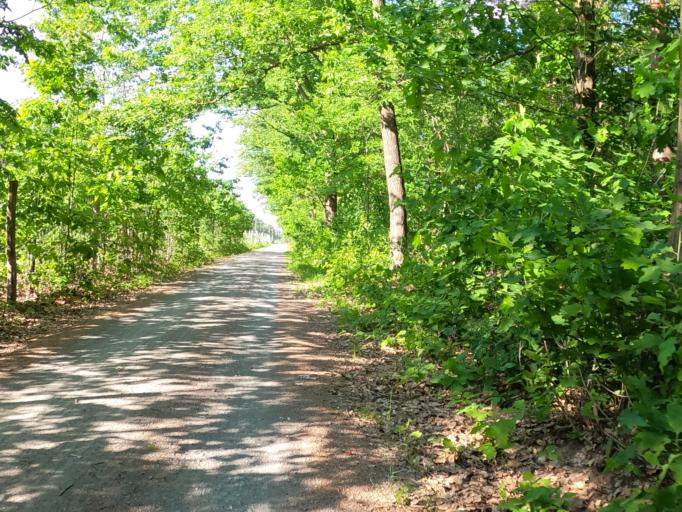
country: DE
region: Hesse
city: Niederrad
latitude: 50.0445
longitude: 8.6111
